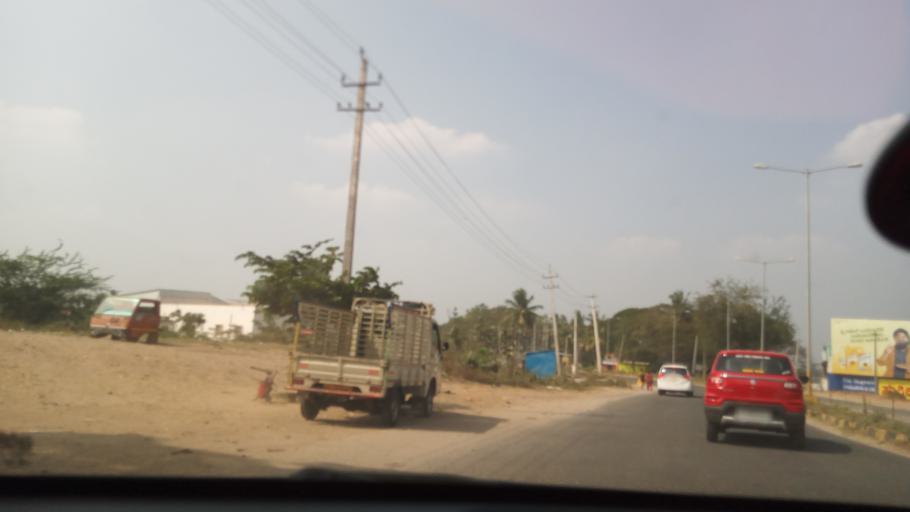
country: IN
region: Karnataka
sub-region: Mysore
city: Nanjangud
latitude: 12.1247
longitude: 76.6826
